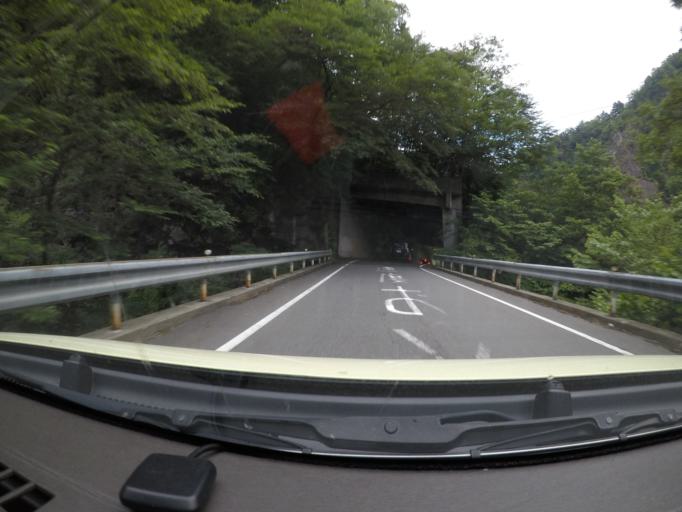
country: JP
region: Tochigi
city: Nikko
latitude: 36.7439
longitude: 139.5182
